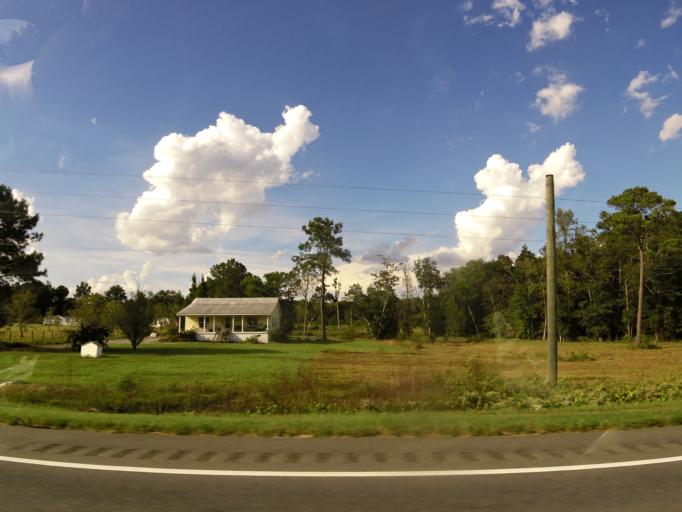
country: US
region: Georgia
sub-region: Brooks County
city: Quitman
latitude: 30.7858
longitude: -83.5998
